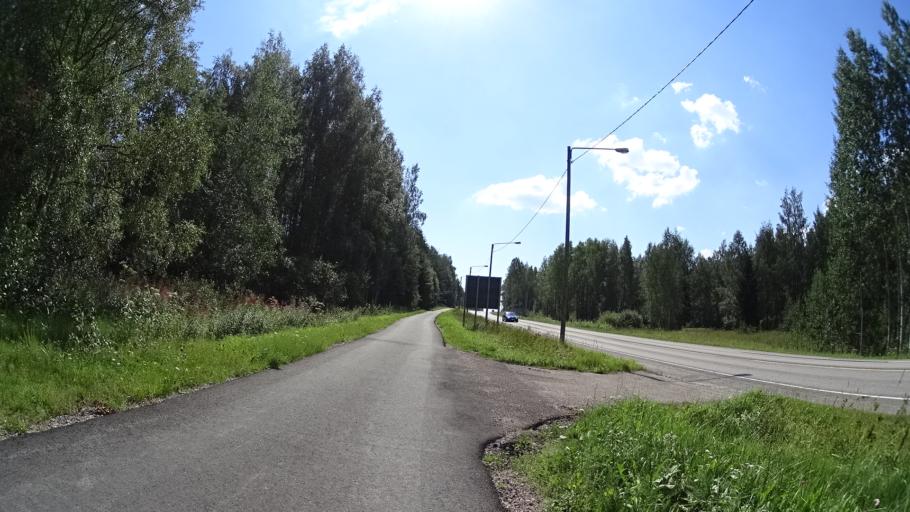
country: FI
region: Uusimaa
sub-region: Helsinki
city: Vantaa
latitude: 60.3221
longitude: 25.0014
